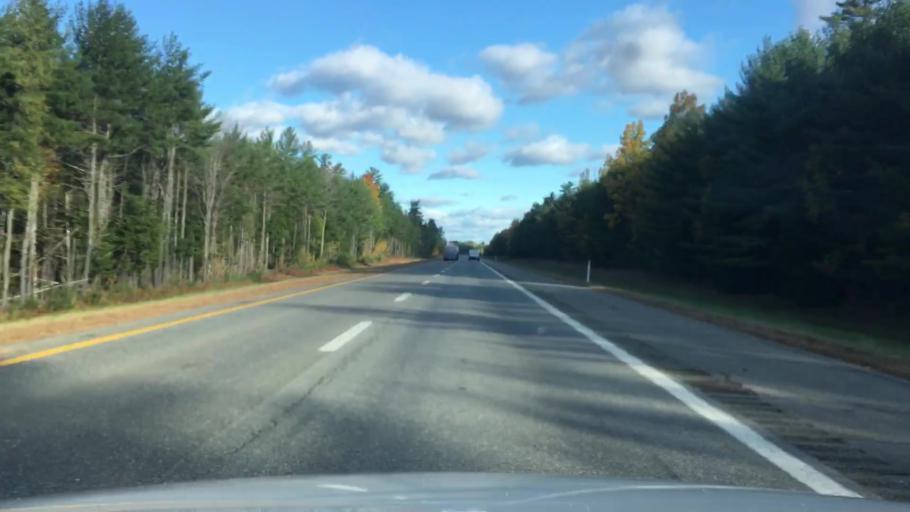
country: US
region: Maine
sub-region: Penobscot County
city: Greenbush
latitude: 45.1365
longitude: -68.6989
